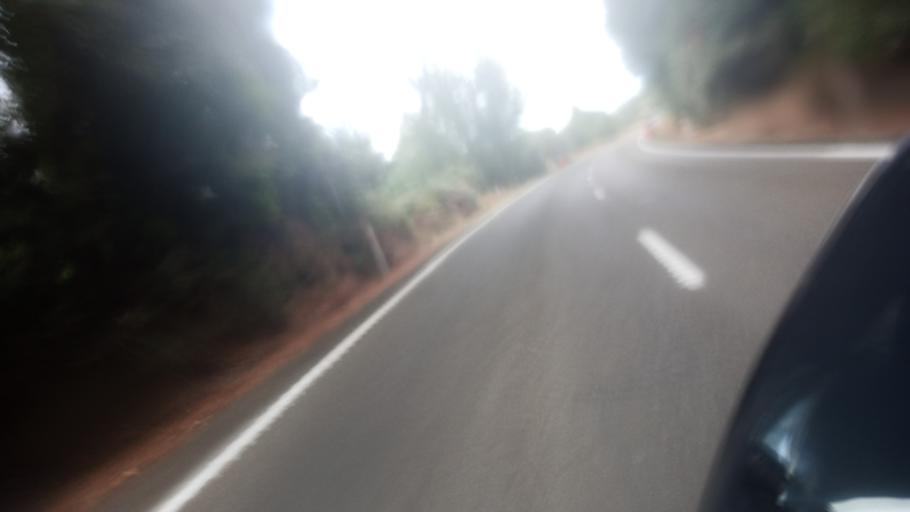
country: NZ
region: Bay of Plenty
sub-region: Opotiki District
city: Opotiki
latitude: -38.4065
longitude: 177.5614
